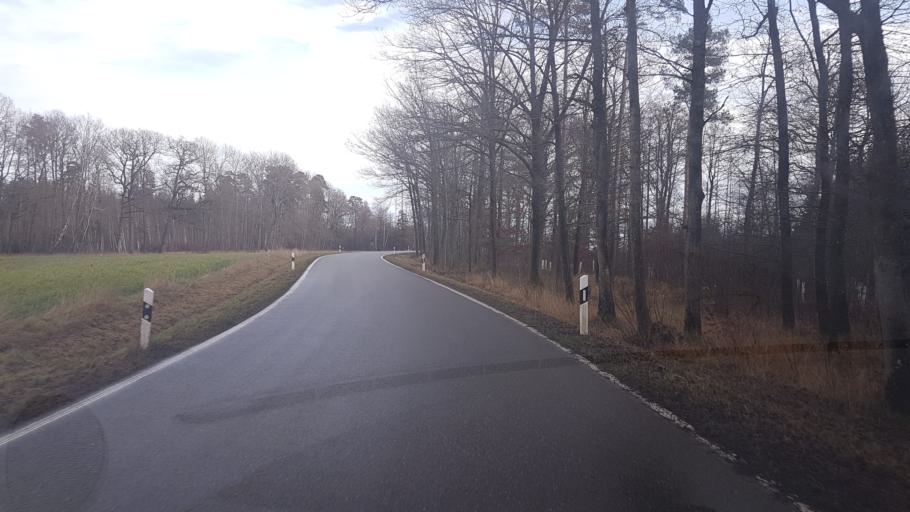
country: DE
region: Baden-Wuerttemberg
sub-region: Regierungsbezirk Stuttgart
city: Wallhausen
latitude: 49.2075
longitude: 10.0336
